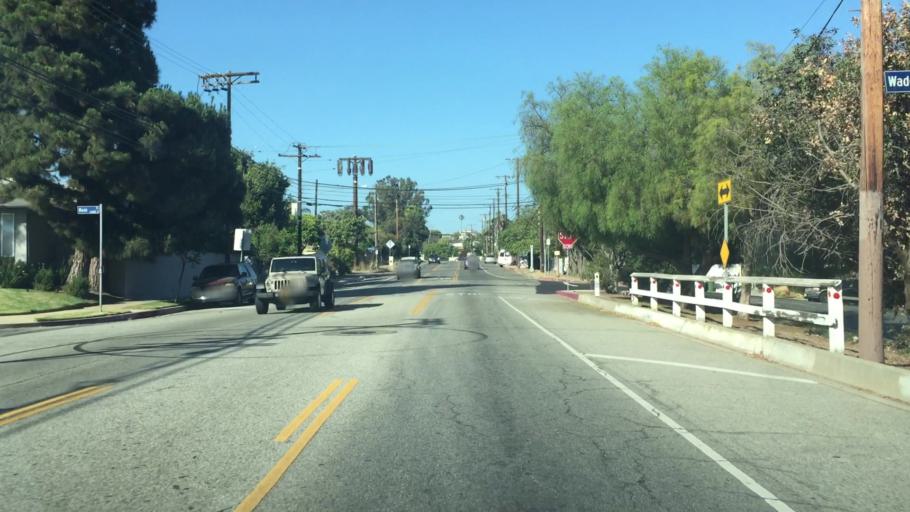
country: US
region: California
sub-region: Los Angeles County
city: Marina del Rey
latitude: 34.0081
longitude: -118.4430
